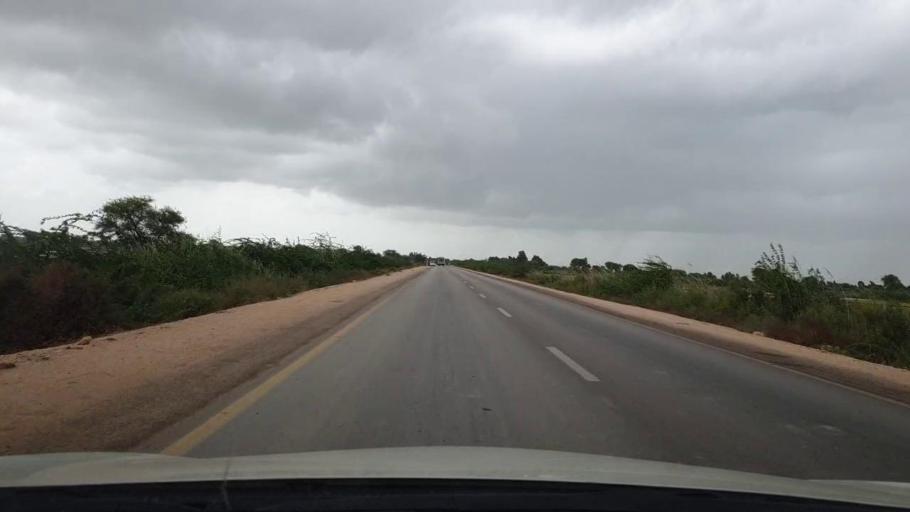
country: PK
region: Sindh
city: Mirpur Batoro
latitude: 24.6428
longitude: 68.4576
